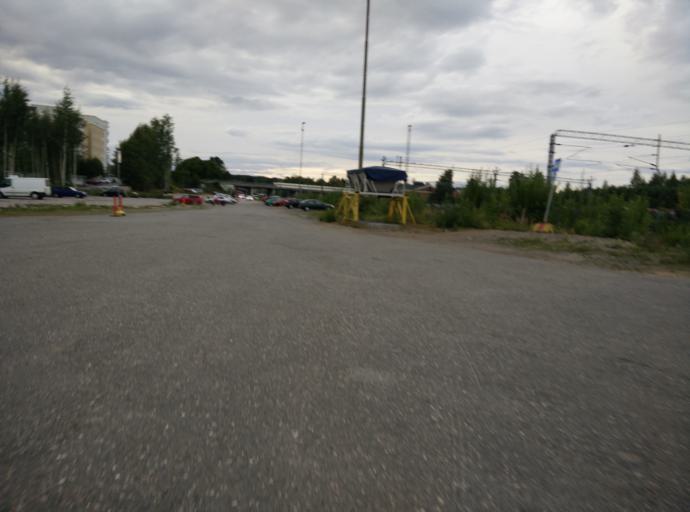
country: FI
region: Haeme
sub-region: Haemeenlinna
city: Haemeenlinna
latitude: 60.9986
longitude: 24.4847
